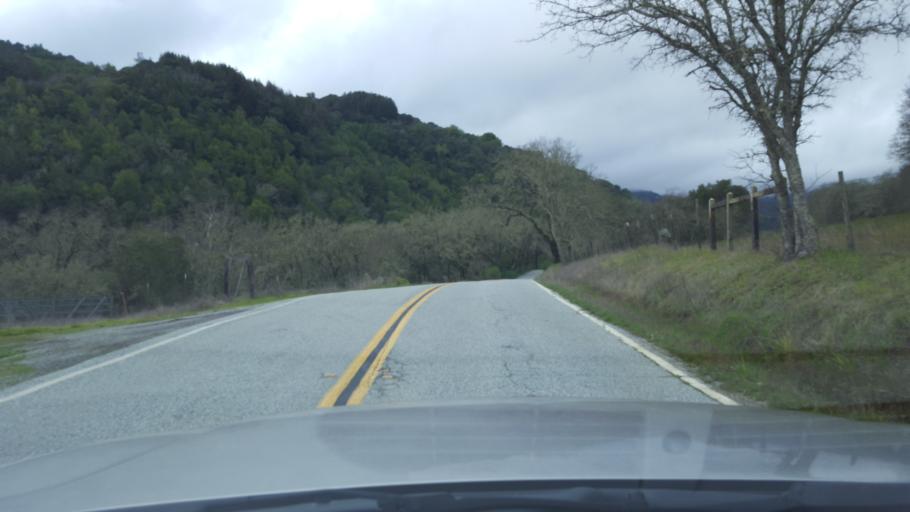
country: US
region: California
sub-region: Santa Cruz County
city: Interlaken
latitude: 37.0303
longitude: -121.6900
